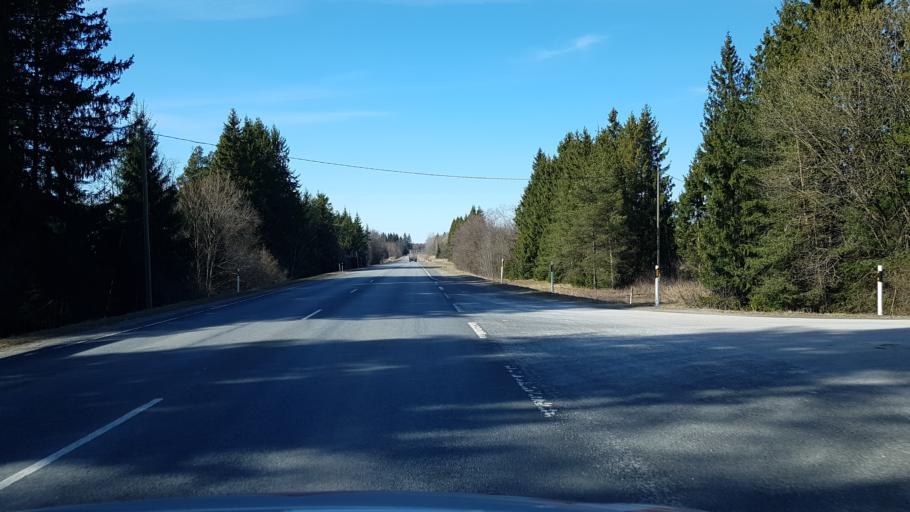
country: EE
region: Harju
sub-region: Nissi vald
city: Turba
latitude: 58.9338
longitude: 24.0971
